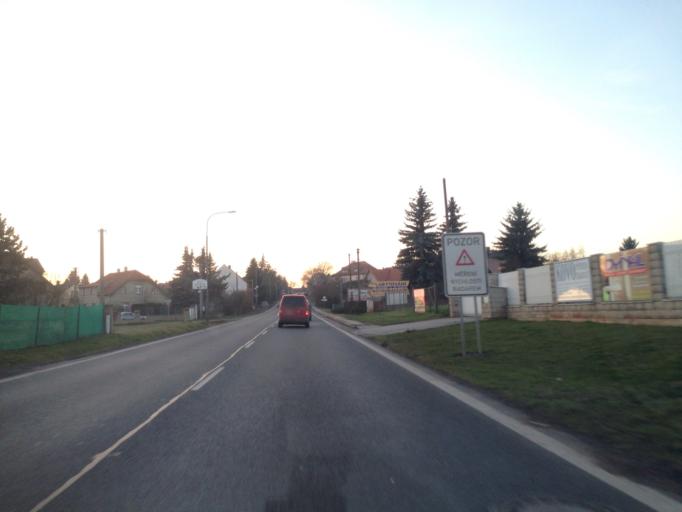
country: CZ
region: Central Bohemia
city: Revnicov
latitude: 50.1803
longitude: 13.8138
